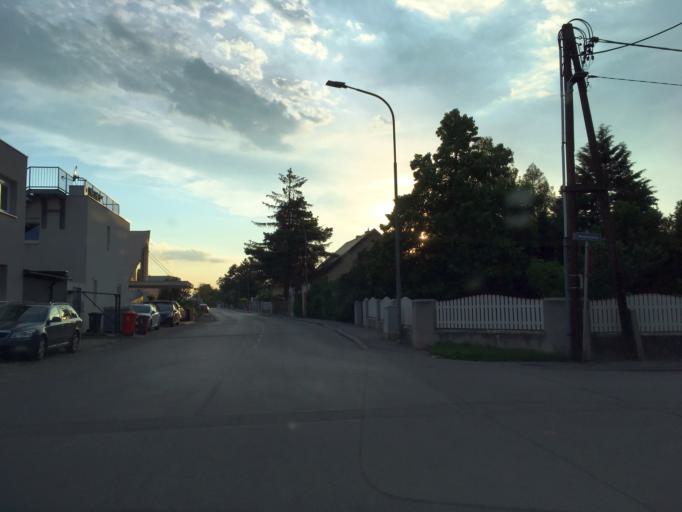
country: AT
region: Lower Austria
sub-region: Politischer Bezirk Wien-Umgebung
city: Gerasdorf bei Wien
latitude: 48.3109
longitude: 16.4967
